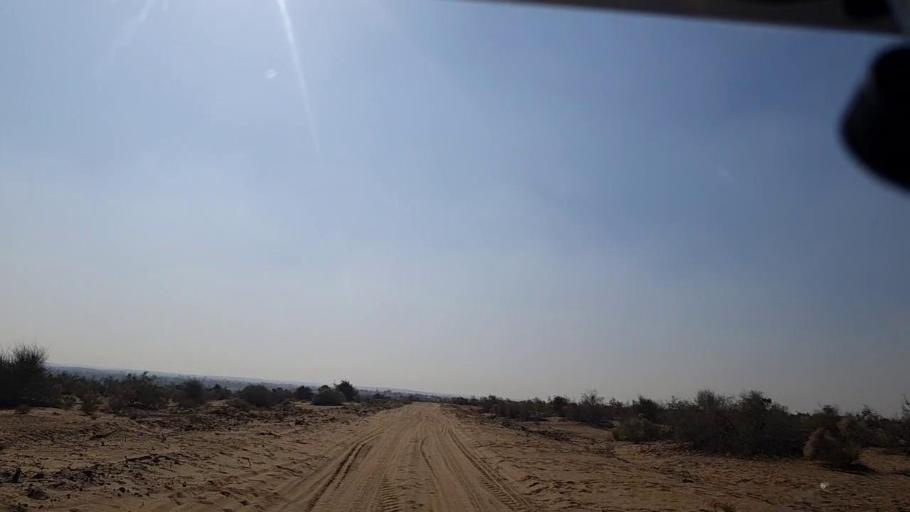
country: PK
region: Sindh
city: Khanpur
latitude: 27.5590
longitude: 69.3875
